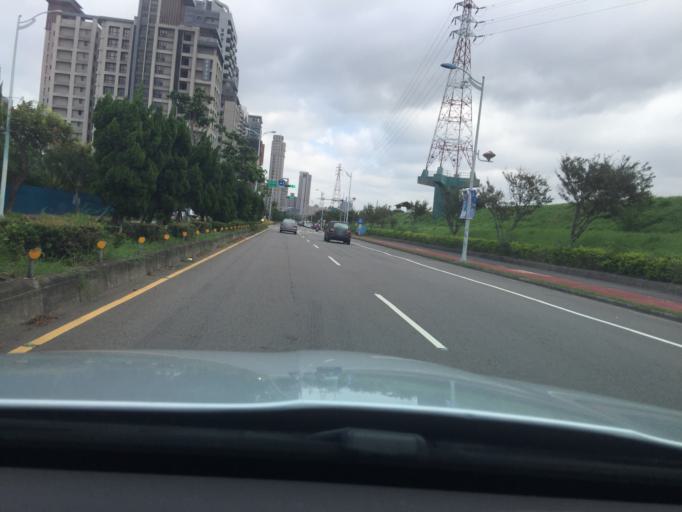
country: TW
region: Taiwan
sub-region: Hsinchu
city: Zhubei
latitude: 24.8216
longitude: 121.0050
